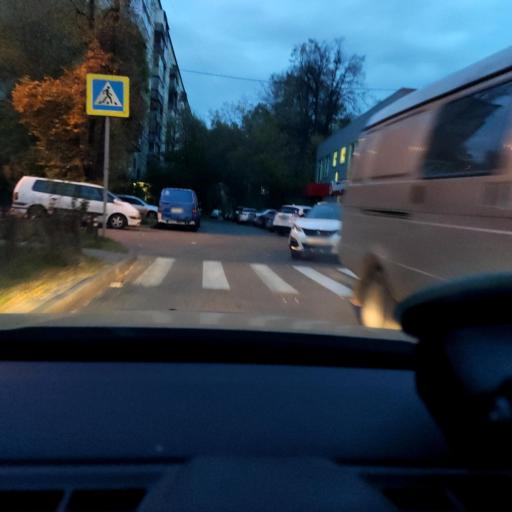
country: RU
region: Moscow
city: Yaroslavskiy
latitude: 55.8927
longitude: 37.7109
